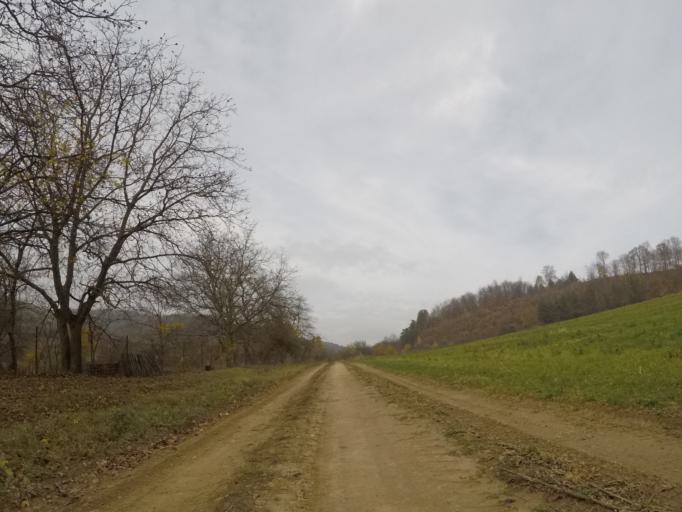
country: SK
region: Presovsky
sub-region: Okres Presov
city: Presov
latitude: 48.9182
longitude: 21.1439
